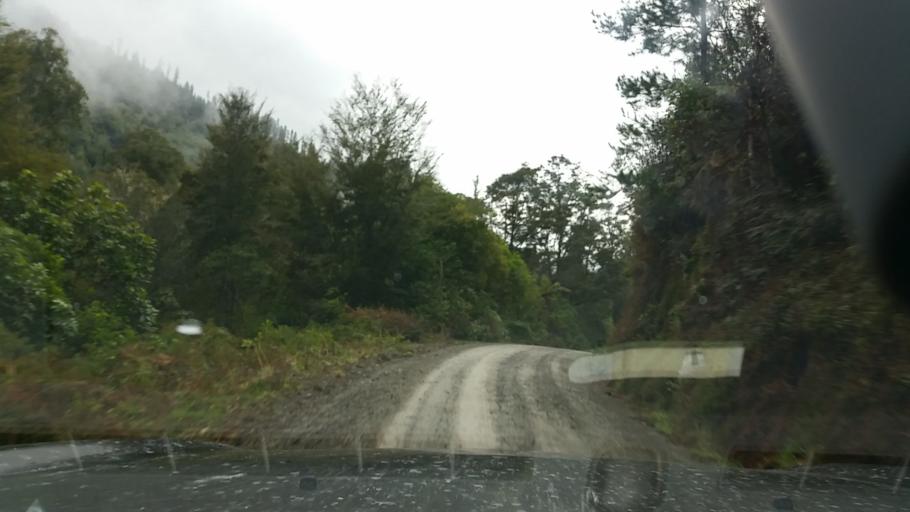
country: NZ
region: Nelson
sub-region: Nelson City
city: Nelson
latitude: -41.3601
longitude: 173.6176
